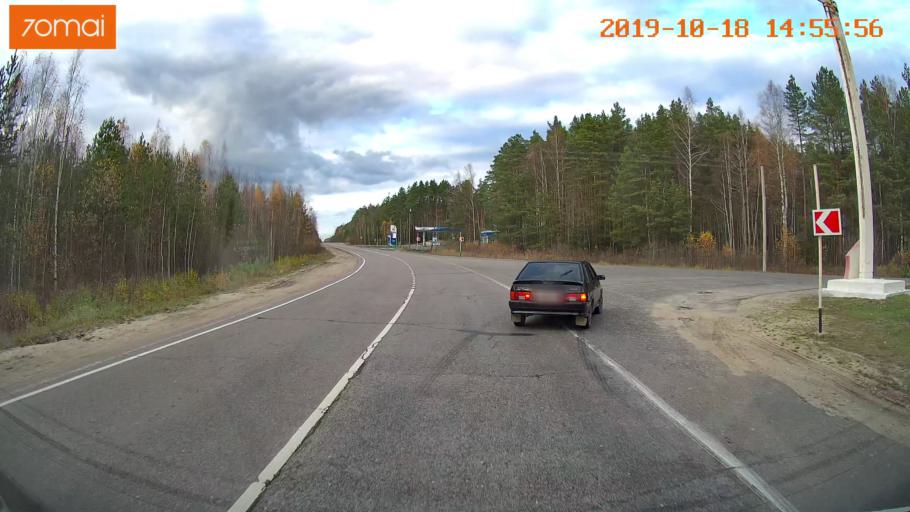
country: RU
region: Vladimir
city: Kurlovo
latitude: 55.4586
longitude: 40.5896
